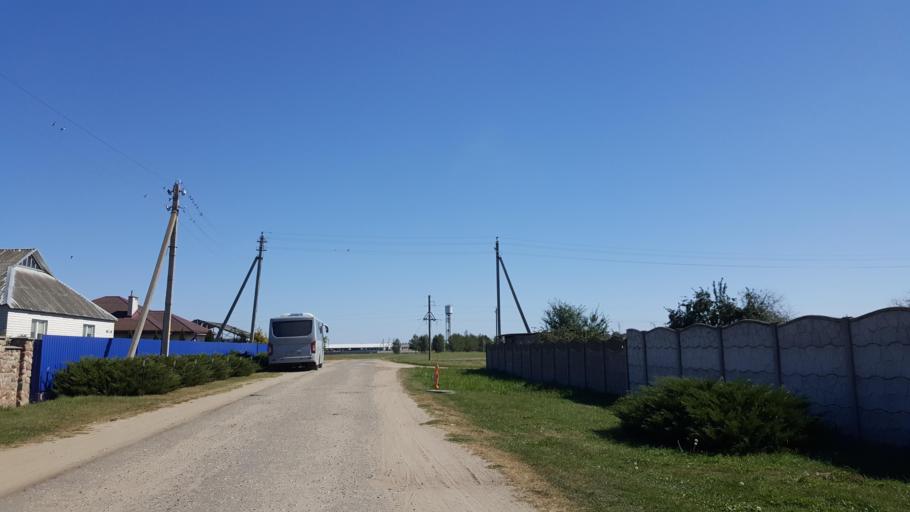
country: BY
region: Brest
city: Vysokaye
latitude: 52.2639
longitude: 23.5009
